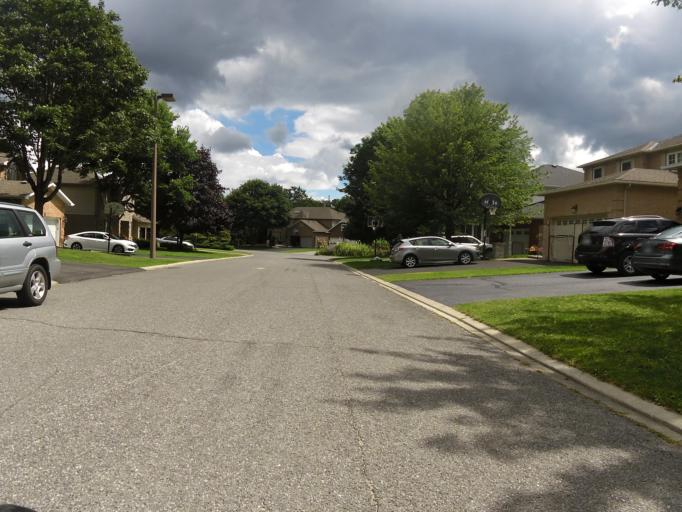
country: CA
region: Ontario
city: Bells Corners
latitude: 45.3187
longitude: -75.9087
